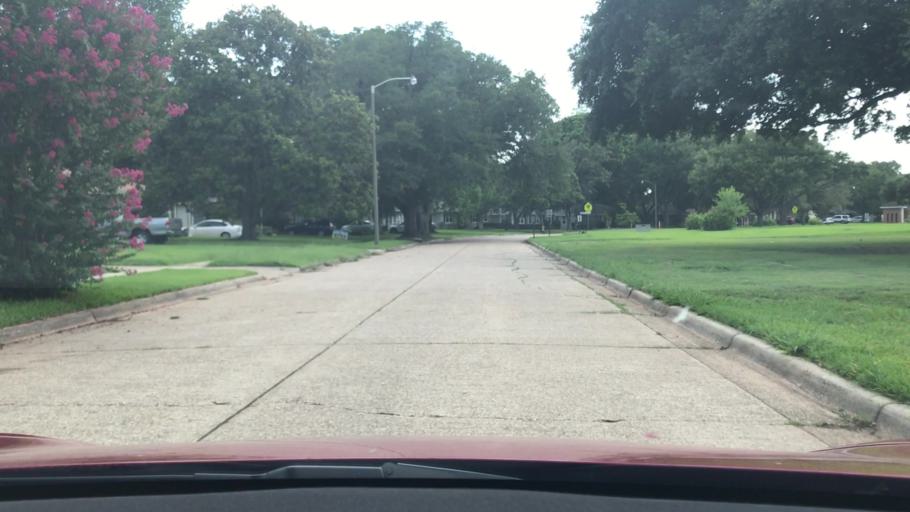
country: US
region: Louisiana
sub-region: Bossier Parish
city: Bossier City
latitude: 32.4585
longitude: -93.7168
